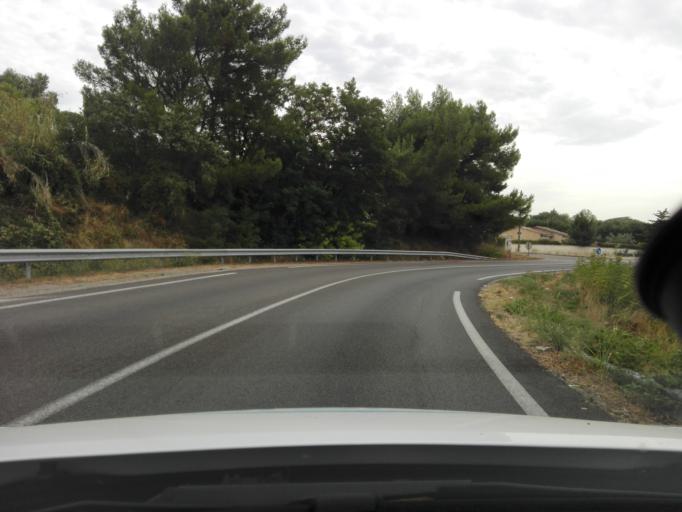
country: FR
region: Languedoc-Roussillon
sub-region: Departement du Gard
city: Villeneuve-les-Avignon
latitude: 43.9498
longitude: 4.7859
